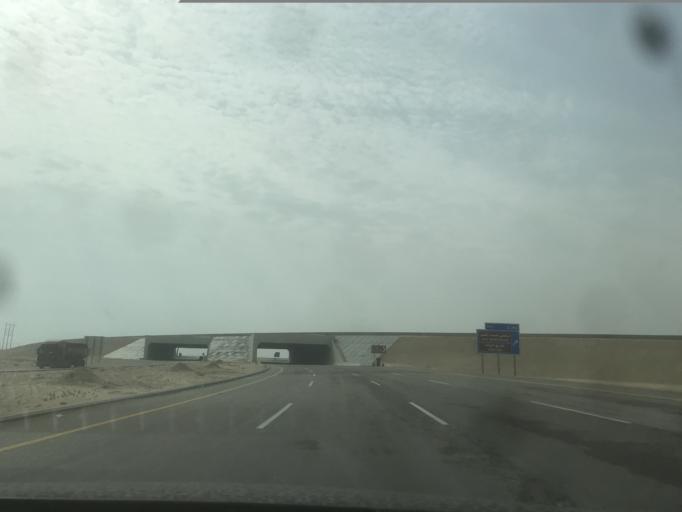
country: SA
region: Eastern Province
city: Dhahran
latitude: 26.1101
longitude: 49.9838
